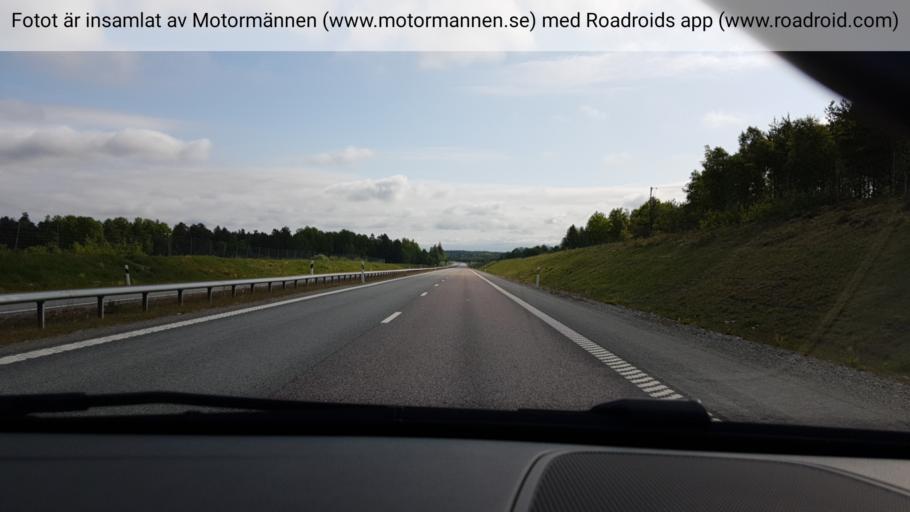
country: SE
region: Stockholm
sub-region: Haninge Kommun
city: Jordbro
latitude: 59.0911
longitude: 18.0930
